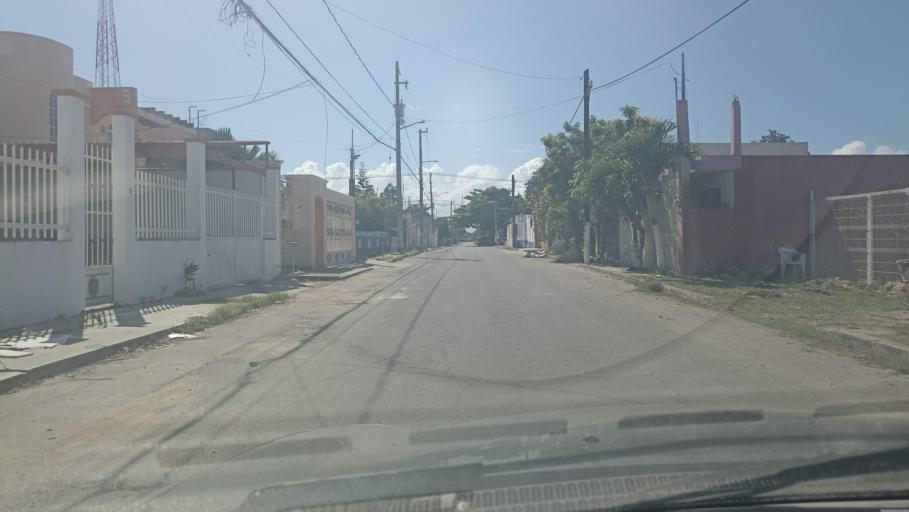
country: MX
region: Quintana Roo
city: Chetumal
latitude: 18.5158
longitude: -88.2855
